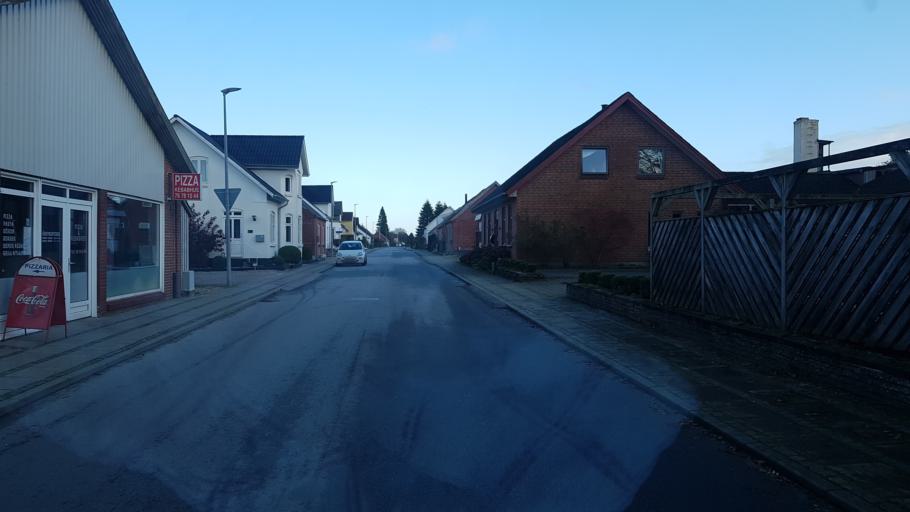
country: DK
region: South Denmark
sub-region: Vejen Kommune
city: Holsted
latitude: 55.4838
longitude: 8.9124
